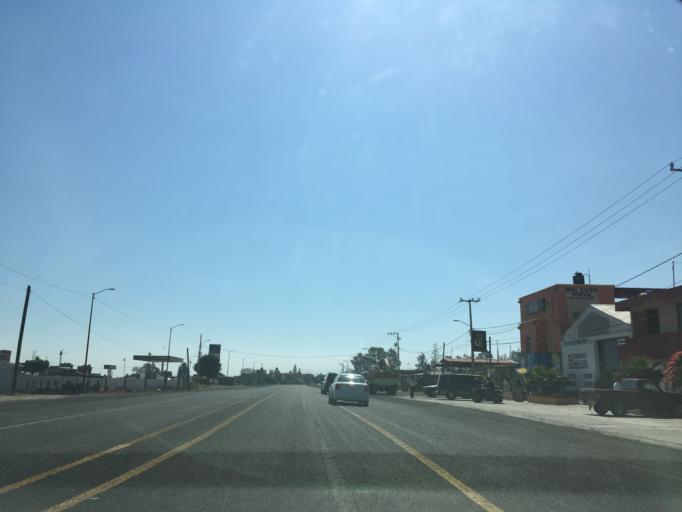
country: MX
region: Michoacan
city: Indaparapeo
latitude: 19.7913
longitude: -100.9720
